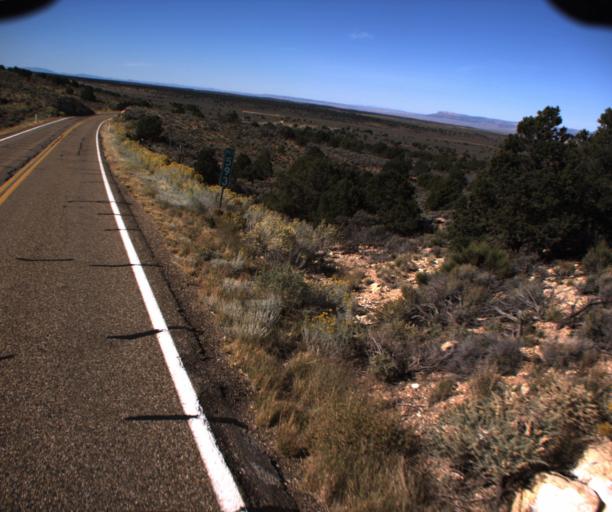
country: US
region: Arizona
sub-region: Coconino County
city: Fredonia
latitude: 36.8461
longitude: -112.2715
